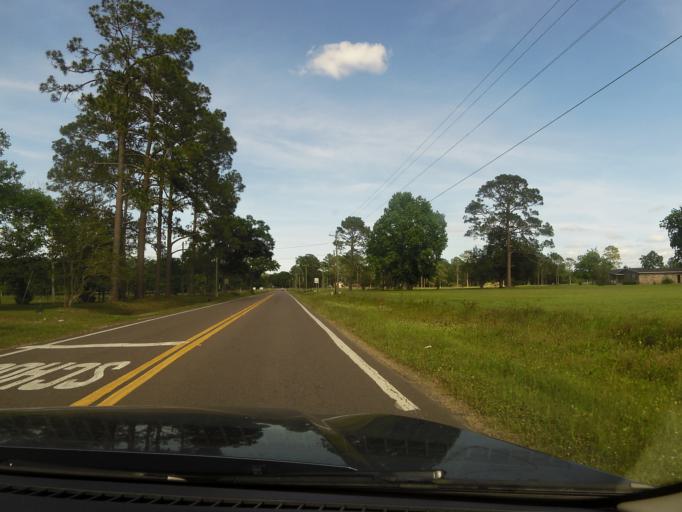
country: US
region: Florida
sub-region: Nassau County
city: Callahan
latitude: 30.5549
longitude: -81.8830
